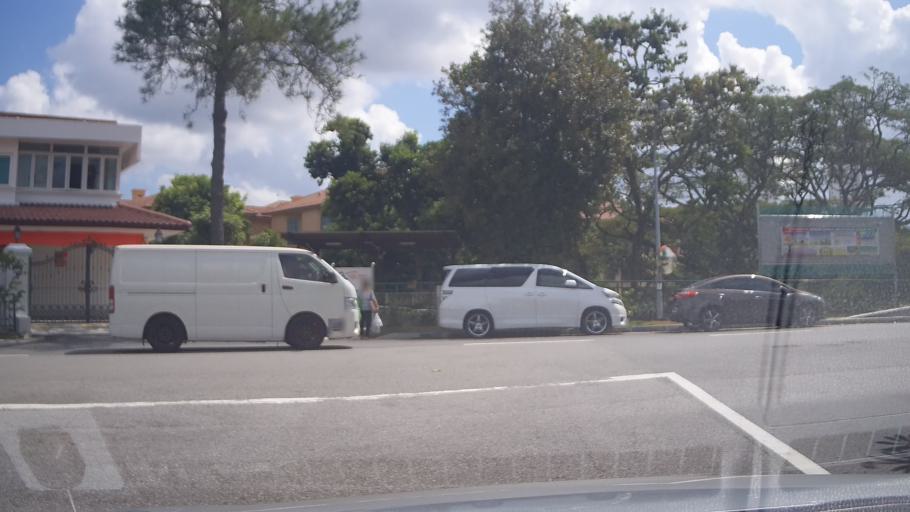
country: SG
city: Singapore
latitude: 1.3225
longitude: 103.7570
